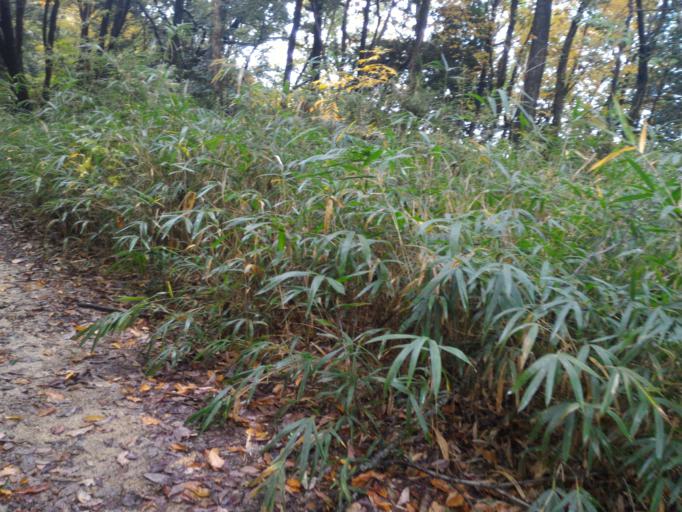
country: JP
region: Osaka
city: Tondabayashicho
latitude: 34.4456
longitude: 135.5667
